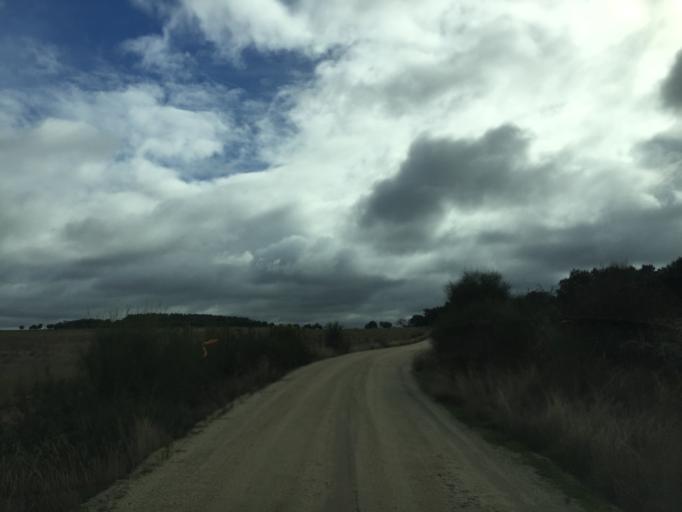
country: PT
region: Portalegre
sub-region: Alter do Chao
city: Alter do Chao
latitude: 39.2389
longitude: -7.6983
